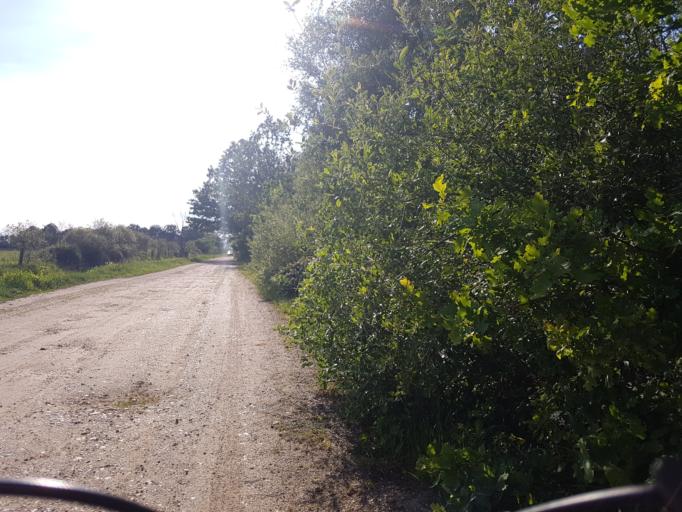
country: DE
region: Brandenburg
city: Merzdorf
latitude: 51.4200
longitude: 13.5436
